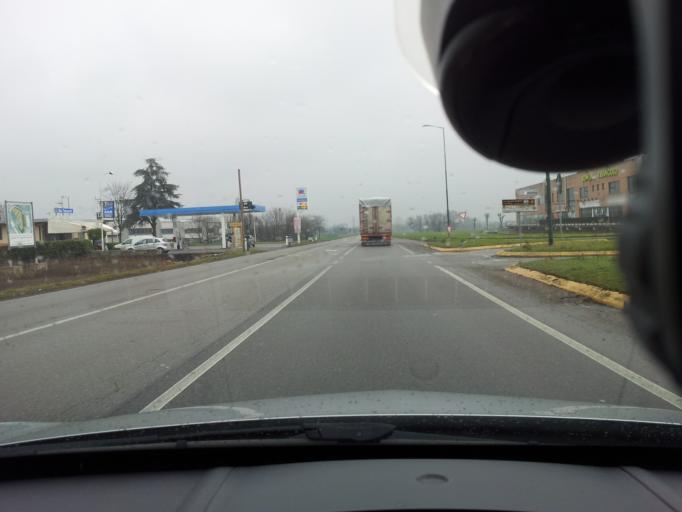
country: IT
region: Lombardy
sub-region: Provincia di Bergamo
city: Cavernago
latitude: 45.6182
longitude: 9.7781
